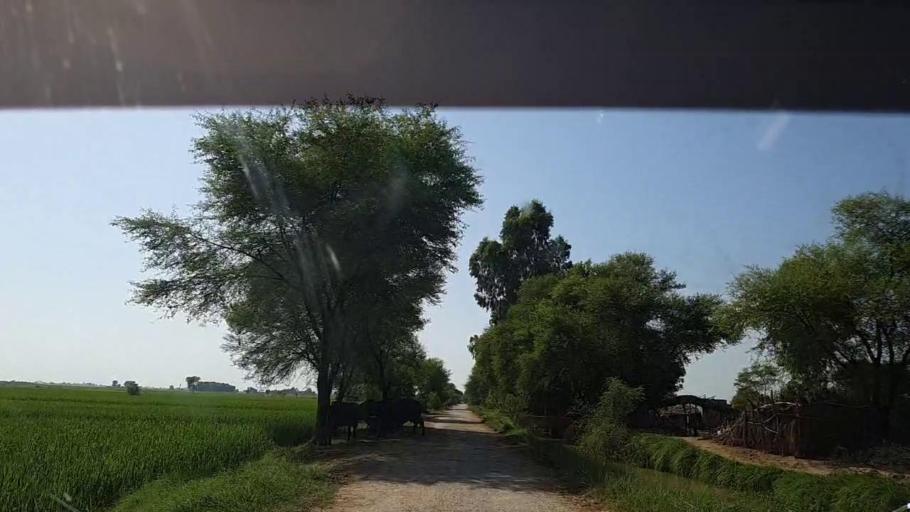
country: PK
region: Sindh
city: Ghauspur
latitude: 28.1775
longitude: 69.0402
